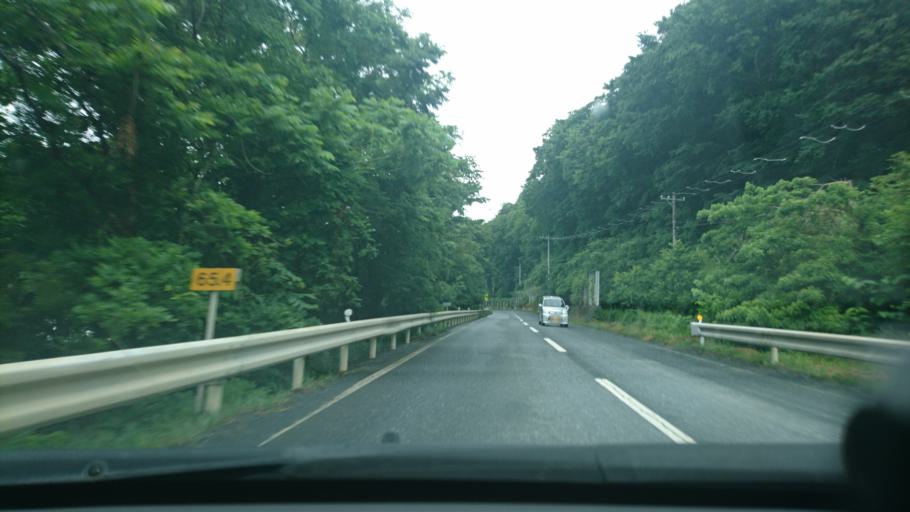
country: JP
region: Miyagi
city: Ishinomaki
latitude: 38.5370
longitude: 141.3069
